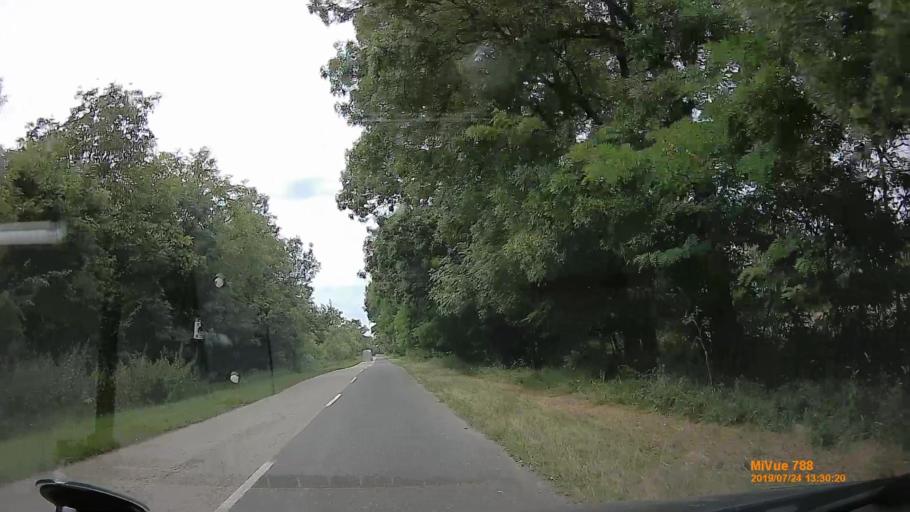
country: HU
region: Szabolcs-Szatmar-Bereg
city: Aranyosapati
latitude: 48.2302
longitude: 22.3811
